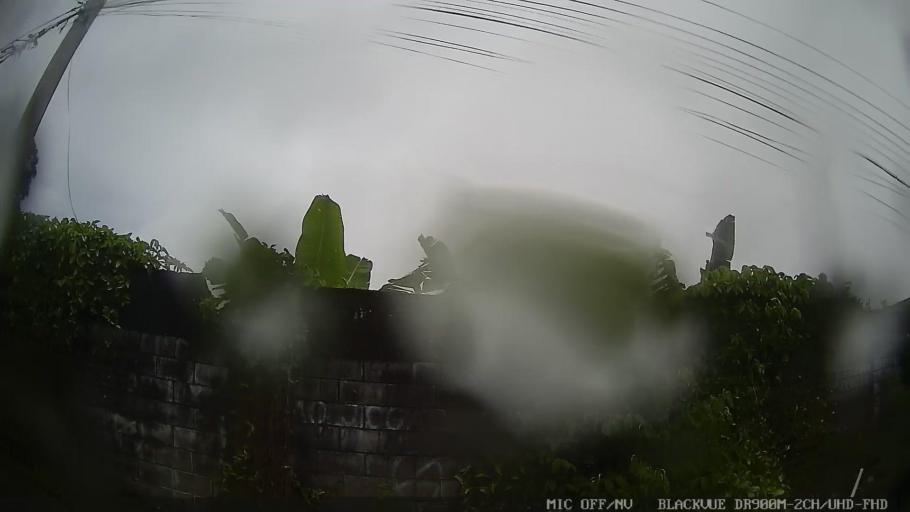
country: BR
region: Sao Paulo
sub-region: Itanhaem
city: Itanhaem
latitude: -24.1875
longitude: -46.8170
